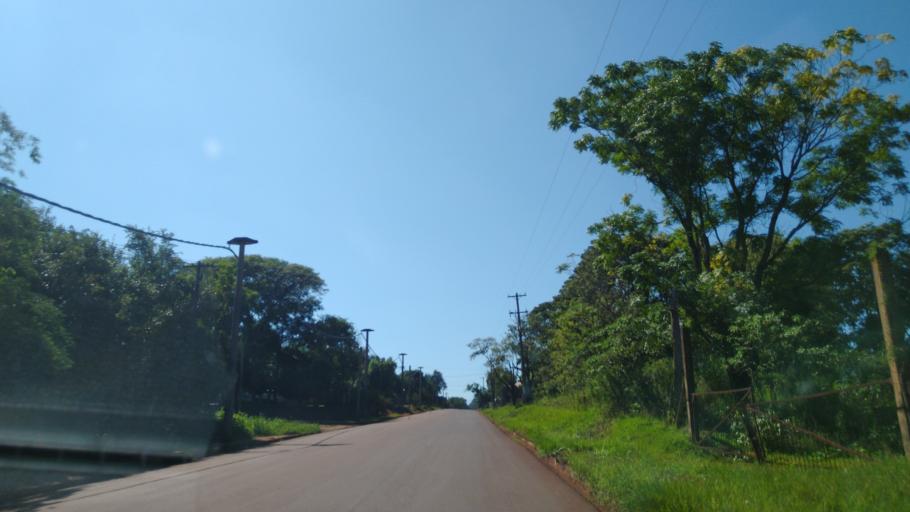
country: AR
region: Misiones
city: Puerto Libertad
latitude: -25.9766
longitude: -54.5777
